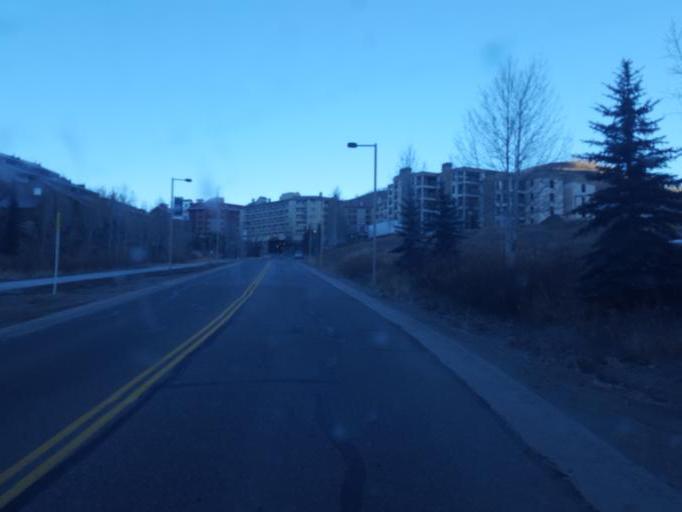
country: US
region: Colorado
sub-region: Gunnison County
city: Crested Butte
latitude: 38.8967
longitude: -106.9685
